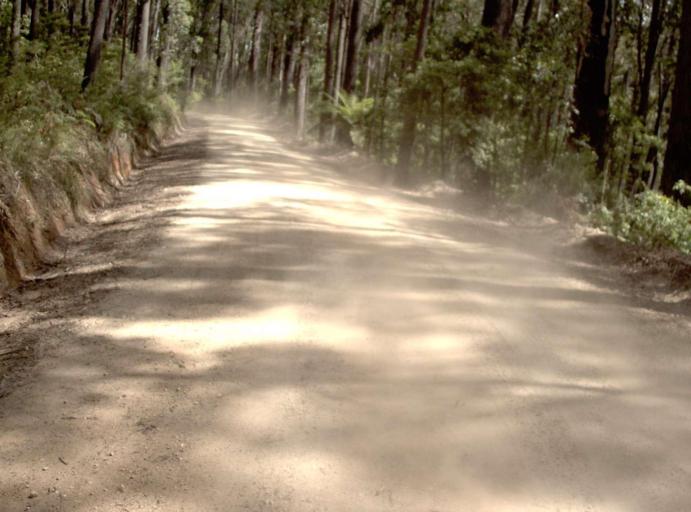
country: AU
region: Victoria
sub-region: East Gippsland
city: Lakes Entrance
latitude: -37.5883
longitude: 148.7246
